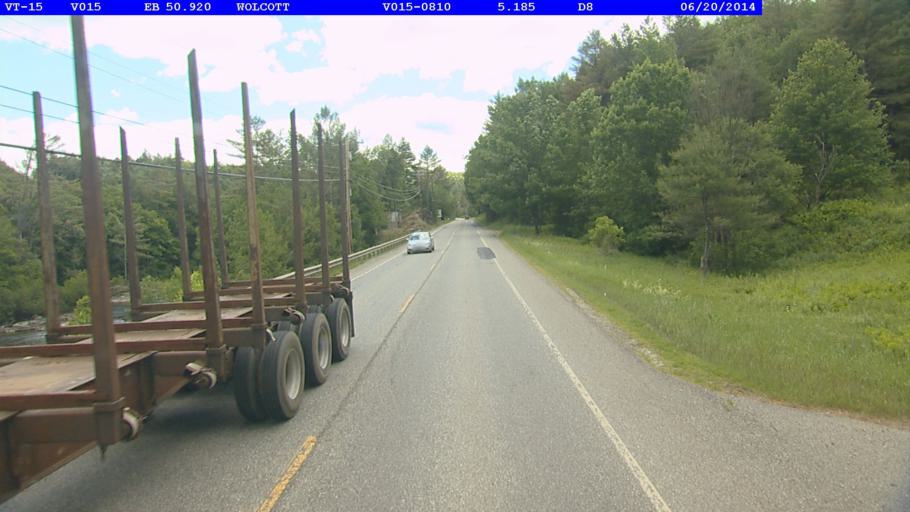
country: US
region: Vermont
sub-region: Caledonia County
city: Hardwick
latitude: 44.5375
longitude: -72.4473
